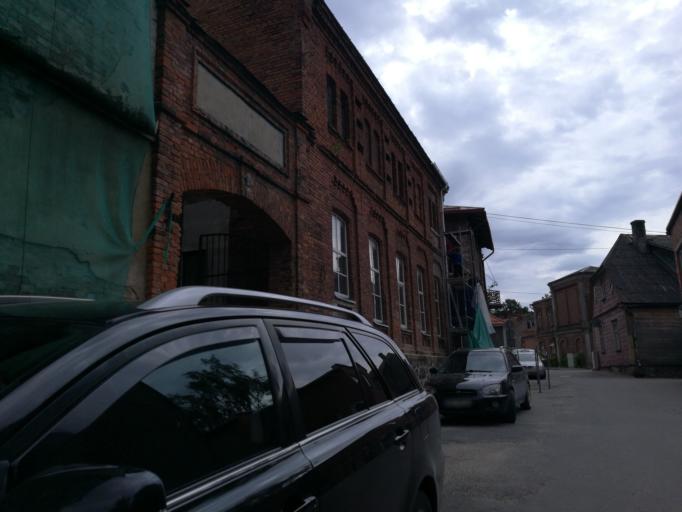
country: LV
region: Limbazu Rajons
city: Limbazi
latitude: 57.5145
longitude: 24.7109
